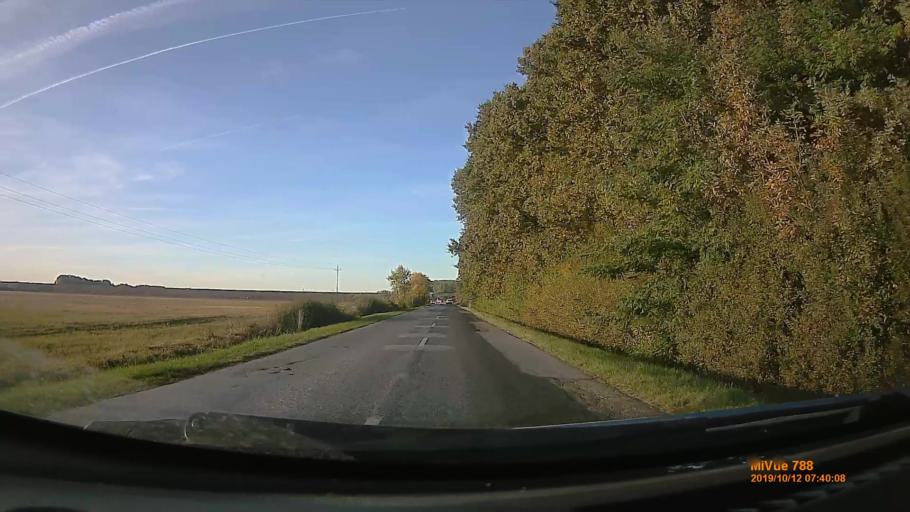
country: HU
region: Hajdu-Bihar
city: Pocsaj
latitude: 47.2080
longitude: 21.7986
